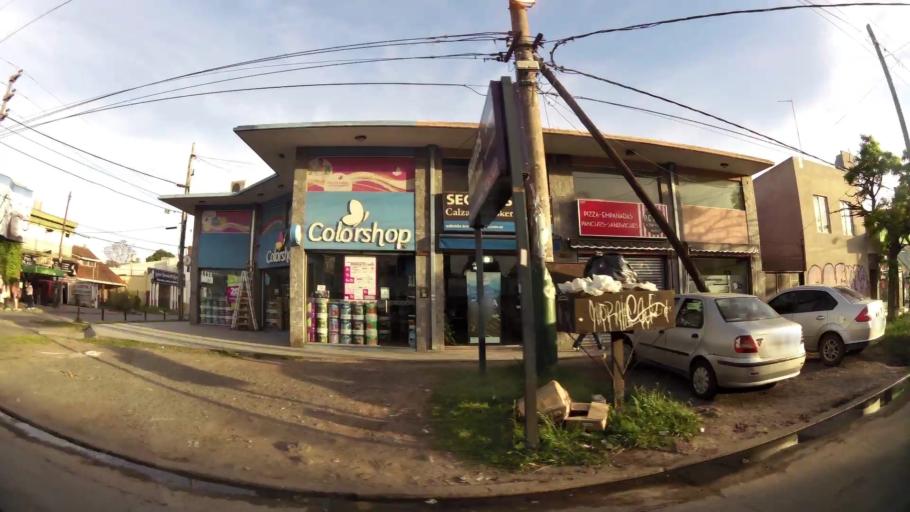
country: AR
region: Buenos Aires
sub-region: Partido de Almirante Brown
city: Adrogue
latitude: -34.7931
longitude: -58.3595
